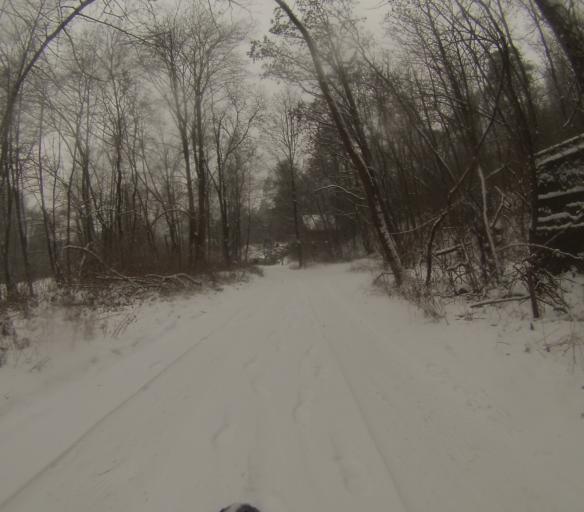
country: CZ
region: South Moravian
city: Orechov
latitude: 49.1349
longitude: 16.5319
